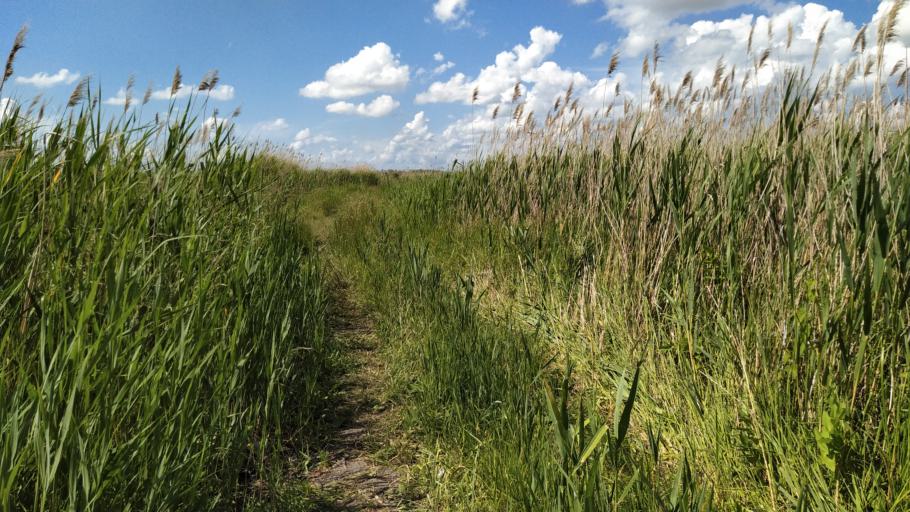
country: RU
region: Rostov
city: Bataysk
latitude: 47.1367
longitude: 39.6699
